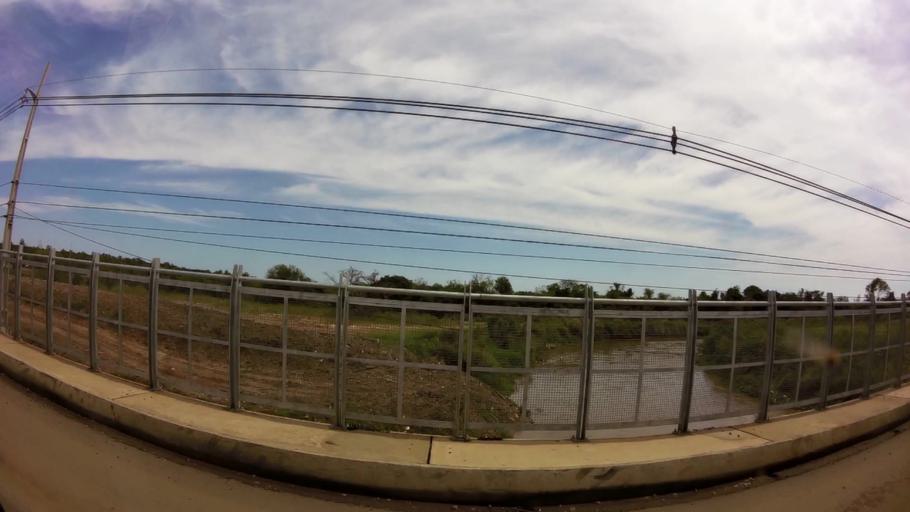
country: PY
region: Central
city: Limpio
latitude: -25.1907
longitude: -57.5017
